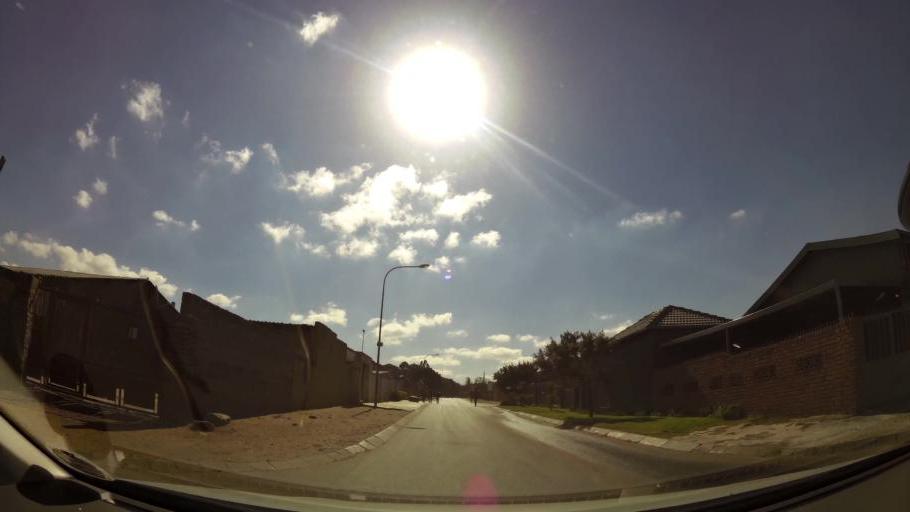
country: ZA
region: Gauteng
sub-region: City of Johannesburg Metropolitan Municipality
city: Roodepoort
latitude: -26.2188
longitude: 27.8951
